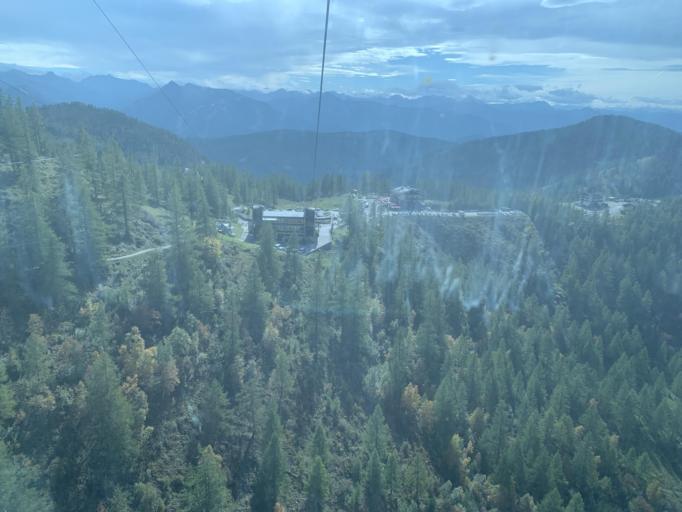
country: AT
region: Styria
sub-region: Politischer Bezirk Liezen
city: Schladming
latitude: 47.4531
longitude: 13.6188
